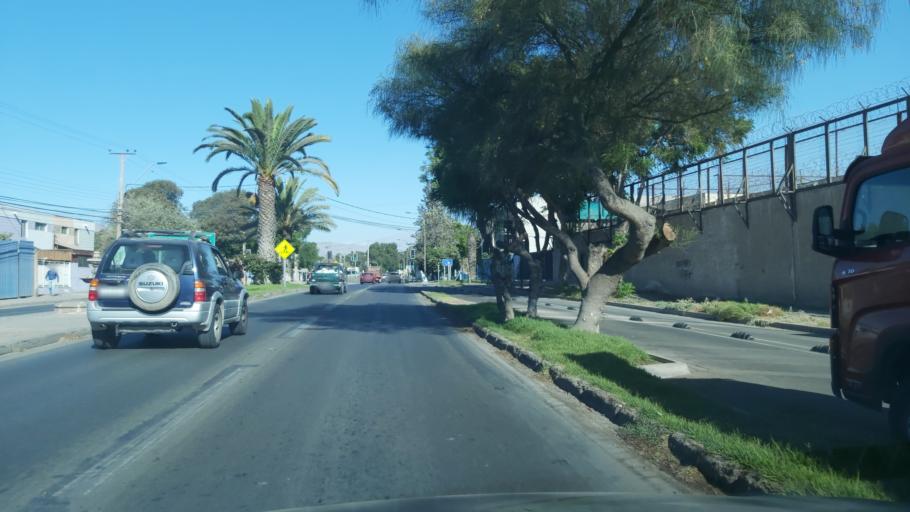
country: CL
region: Atacama
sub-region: Provincia de Copiapo
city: Copiapo
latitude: -27.3728
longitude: -70.3299
